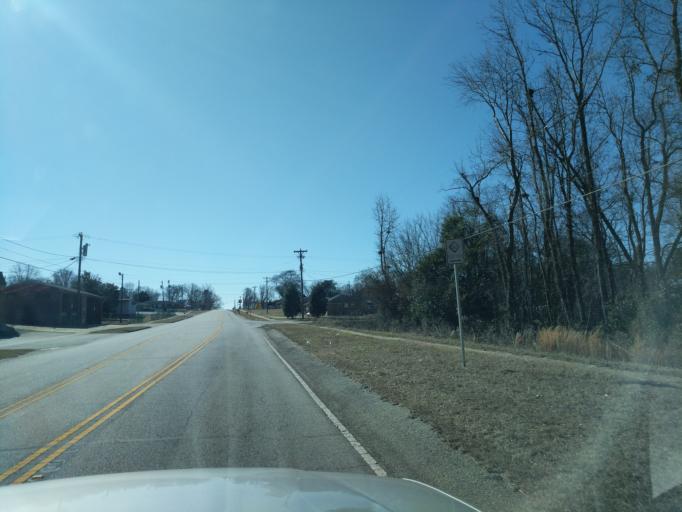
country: US
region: South Carolina
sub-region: Anderson County
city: Anderson
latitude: 34.4897
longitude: -82.6556
